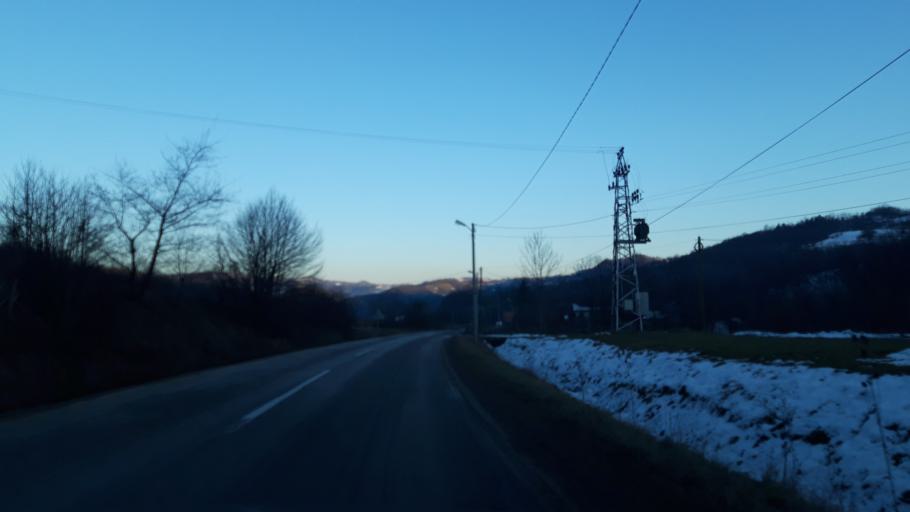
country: BA
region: Republika Srpska
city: Milici
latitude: 44.1646
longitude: 19.0435
